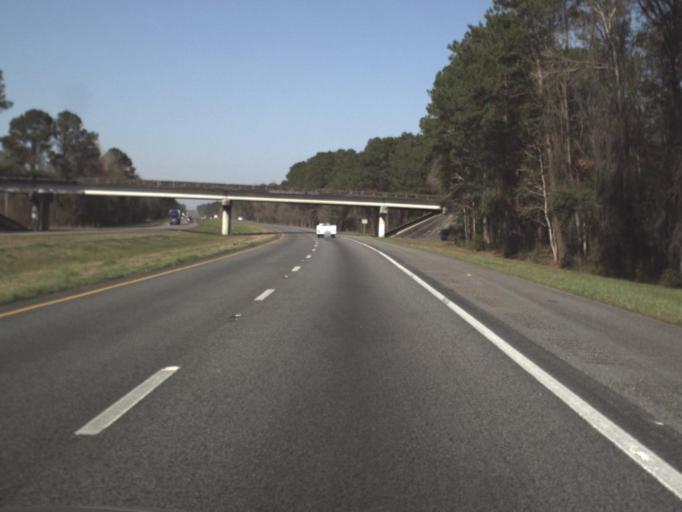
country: US
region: Florida
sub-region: Jefferson County
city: Monticello
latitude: 30.4724
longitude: -83.8217
